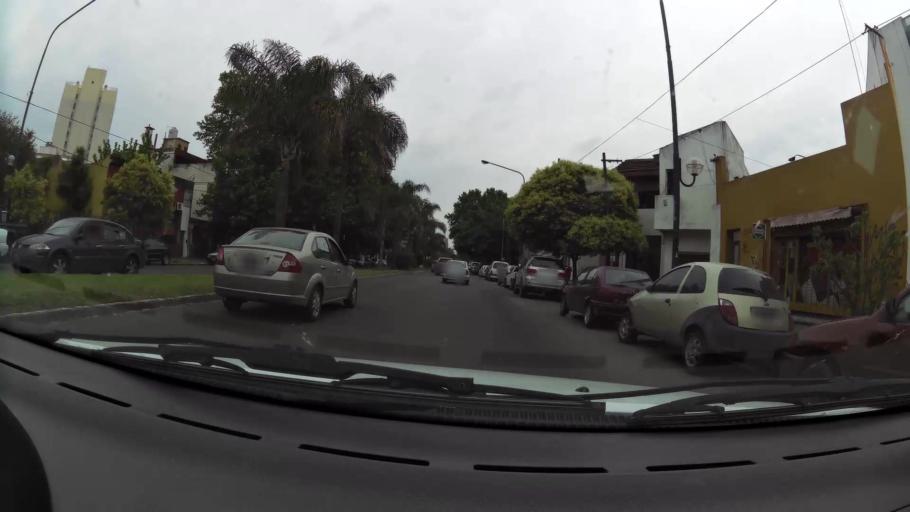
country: AR
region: Buenos Aires
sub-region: Partido de La Plata
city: La Plata
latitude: -34.9298
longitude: -57.9540
